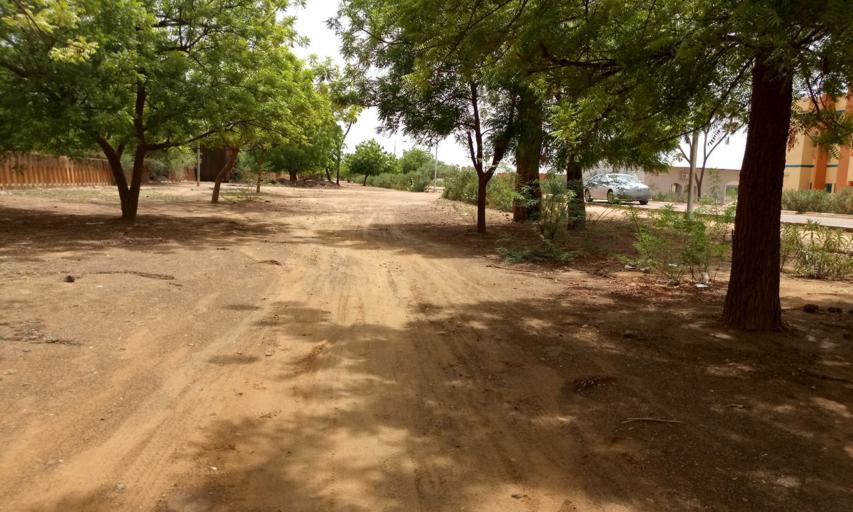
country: NE
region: Niamey
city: Niamey
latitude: 13.5021
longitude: 2.0897
